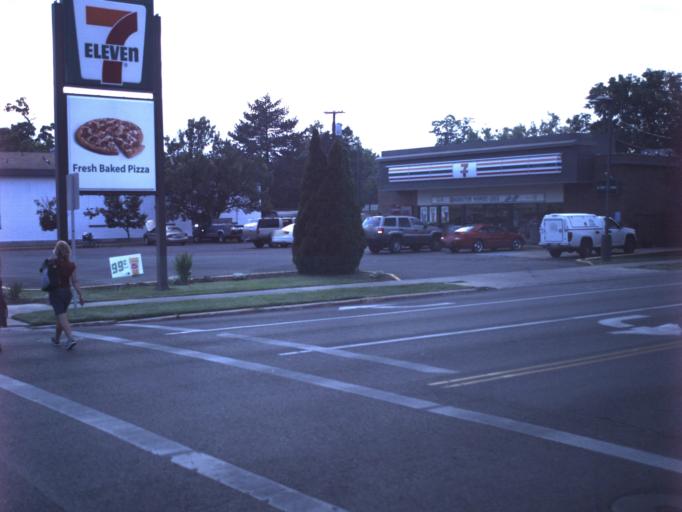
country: US
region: Utah
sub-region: Utah County
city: Provo
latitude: 40.2298
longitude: -111.6621
